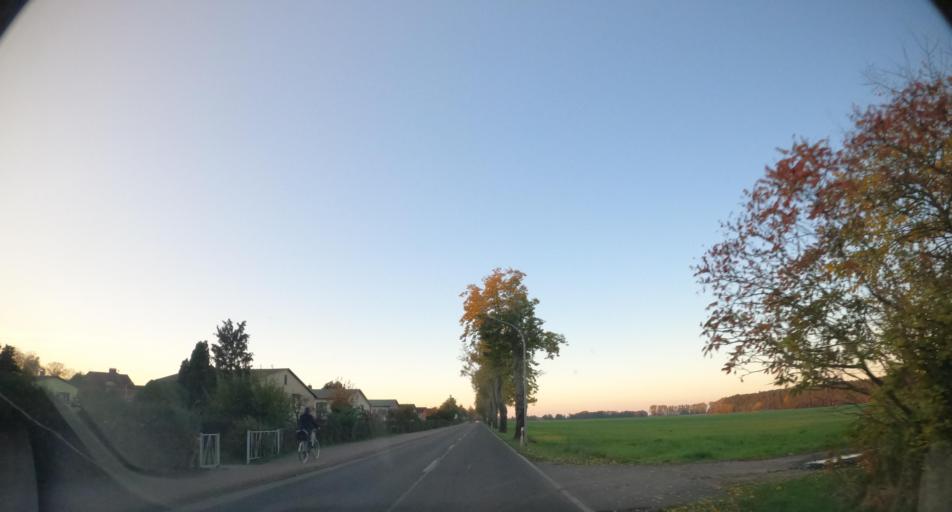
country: DE
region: Mecklenburg-Vorpommern
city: Ueckermunde
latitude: 53.7432
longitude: 14.0330
